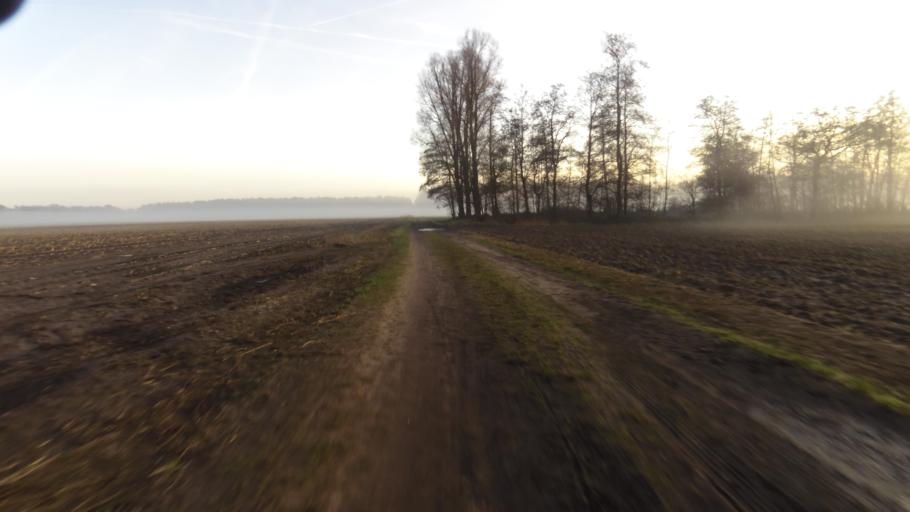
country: NL
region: Gelderland
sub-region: Gemeente Apeldoorn
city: Uddel
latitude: 52.2428
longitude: 5.7860
